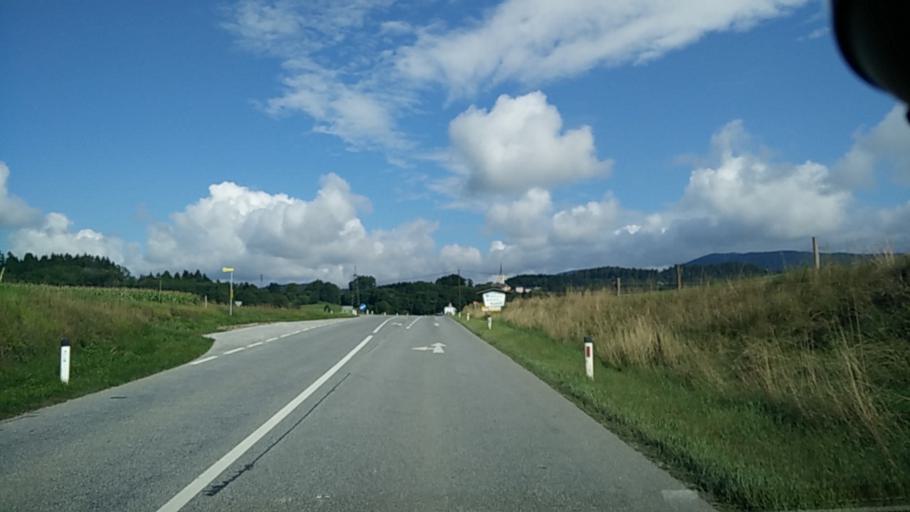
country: AT
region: Carinthia
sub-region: Politischer Bezirk Volkermarkt
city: Gallizien
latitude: 46.6229
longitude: 14.5466
